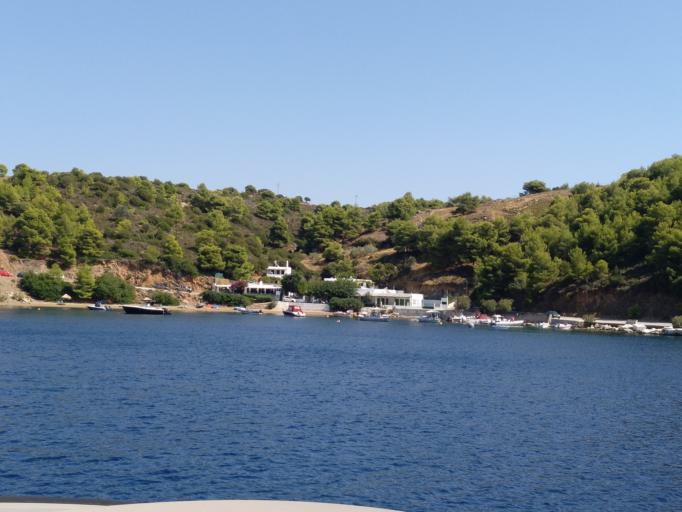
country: GR
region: Central Greece
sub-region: Nomos Evvoias
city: Skyros
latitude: 38.8556
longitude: 24.5090
